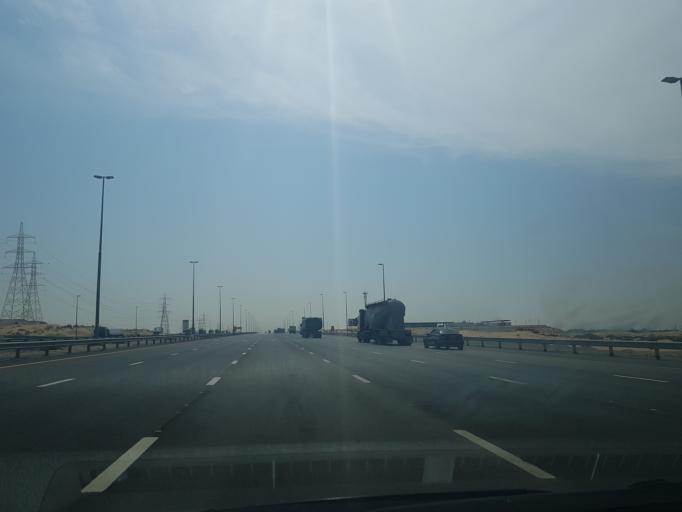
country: AE
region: Ash Shariqah
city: Sharjah
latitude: 25.2598
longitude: 55.5759
